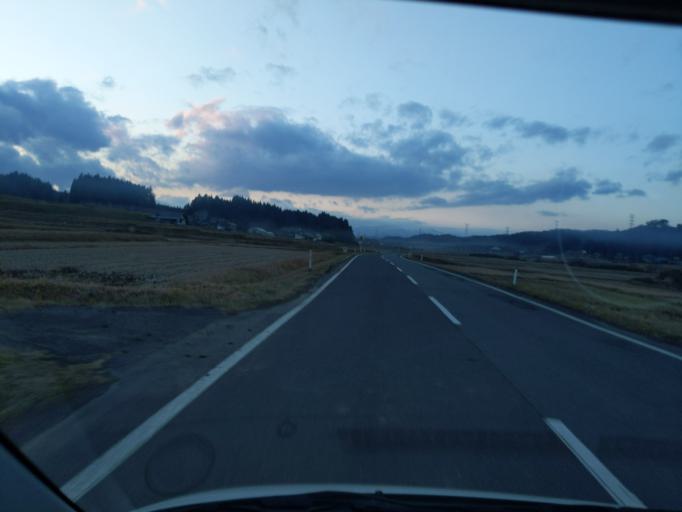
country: JP
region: Iwate
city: Ichinoseki
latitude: 38.8422
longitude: 141.1220
